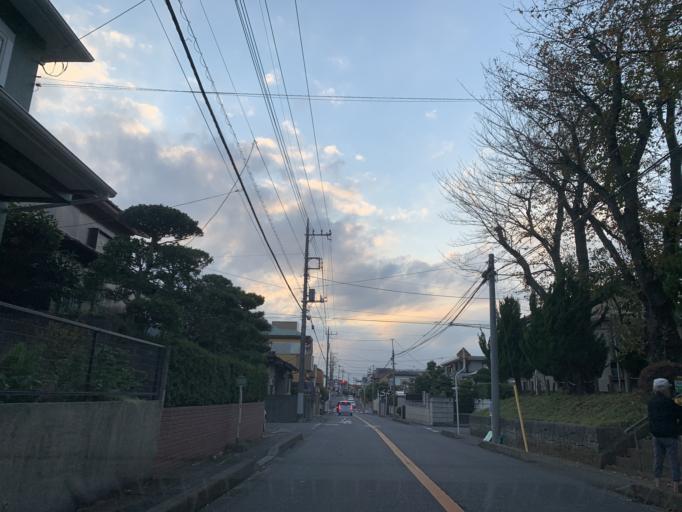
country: JP
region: Chiba
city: Nagareyama
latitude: 35.8924
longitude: 139.9075
